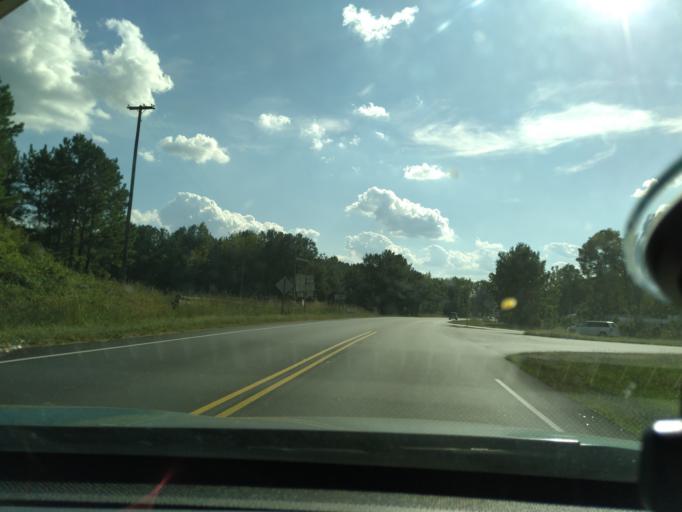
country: US
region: North Carolina
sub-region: Nash County
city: Sharpsburg
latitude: 35.9127
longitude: -77.8309
